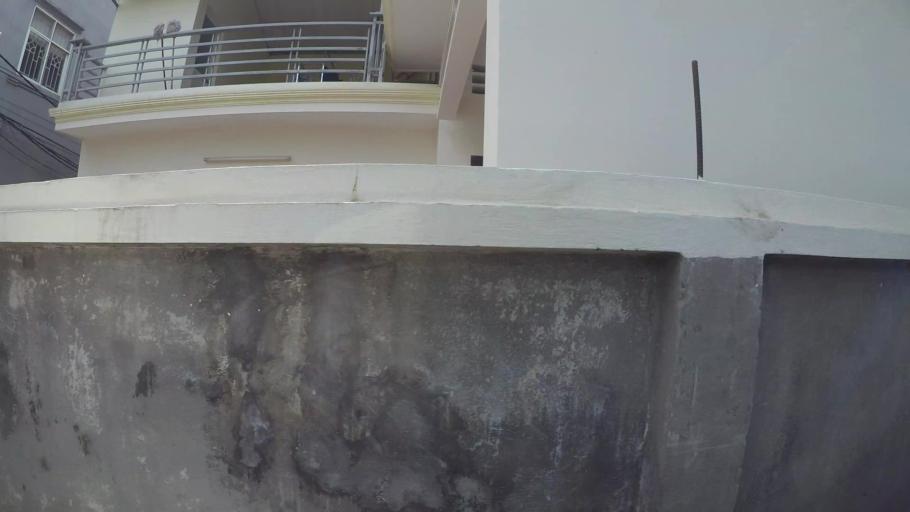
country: VN
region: Ha Noi
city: Tay Ho
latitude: 21.0873
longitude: 105.8001
